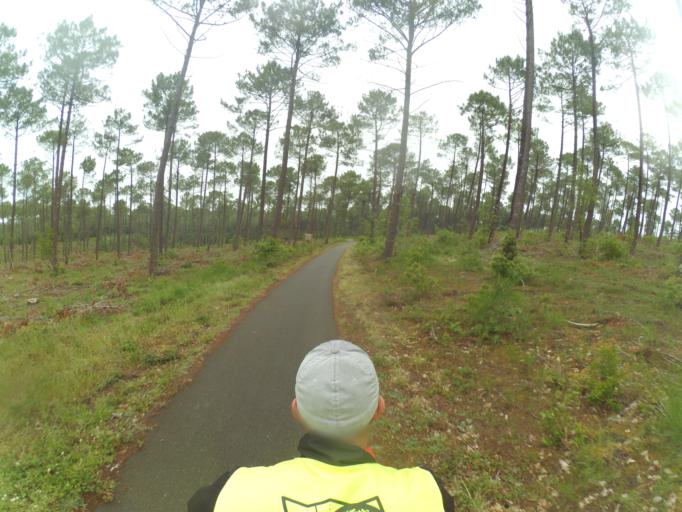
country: FR
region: Aquitaine
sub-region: Departement des Landes
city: Mimizan
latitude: 44.2193
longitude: -1.2509
